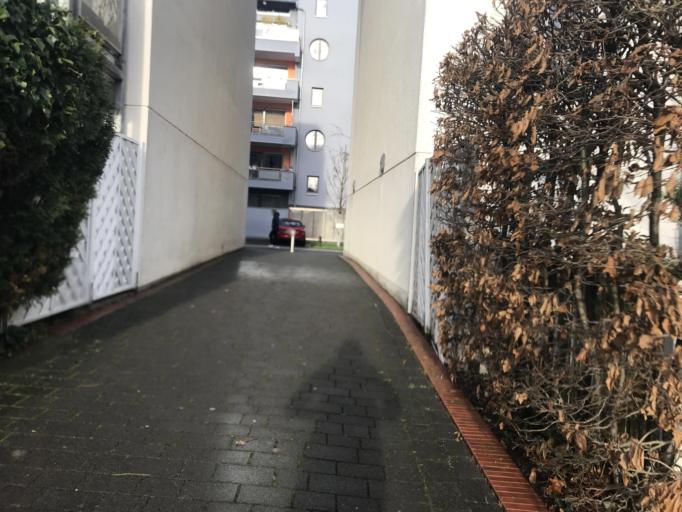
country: DE
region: Rheinland-Pfalz
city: Budenheim
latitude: 50.0087
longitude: 8.2180
